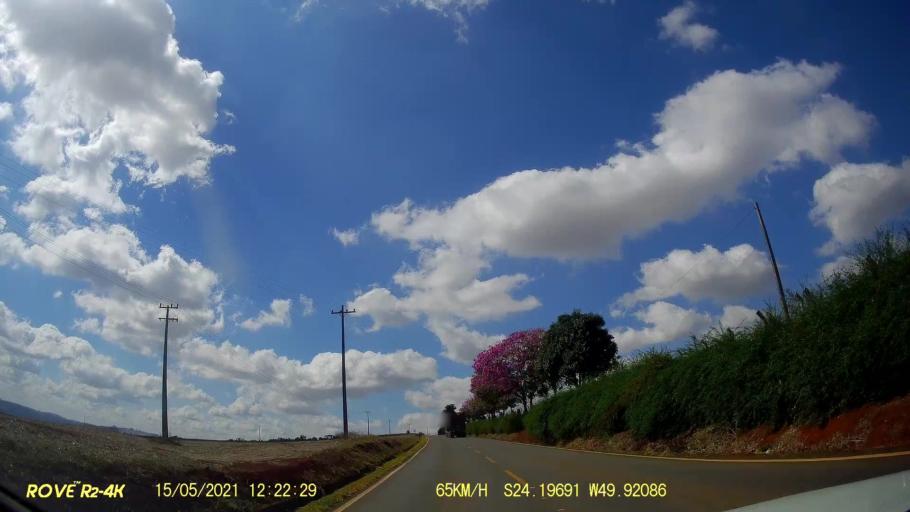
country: BR
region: Parana
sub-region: Jaguariaiva
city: Jaguariaiva
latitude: -24.1969
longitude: -49.9209
